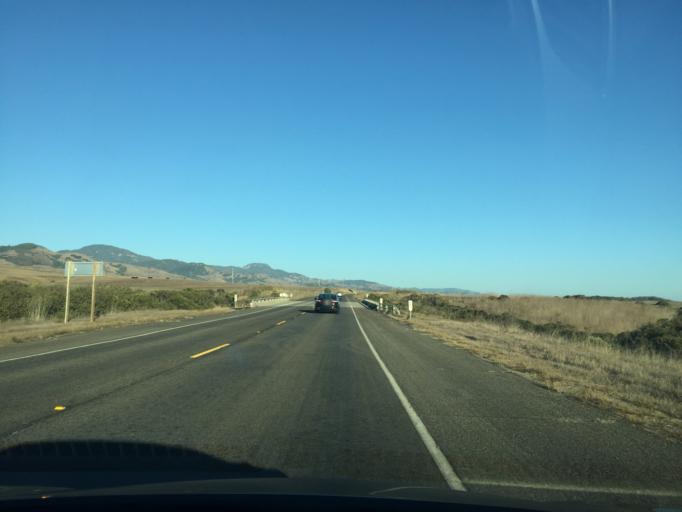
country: US
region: California
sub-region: San Luis Obispo County
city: Cambria
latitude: 35.6532
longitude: -121.2204
